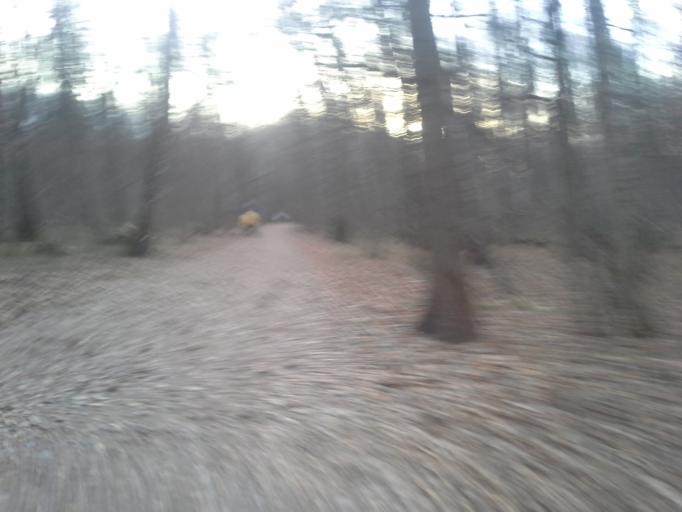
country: RU
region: Moscow
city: Chertanovo Yuzhnoye
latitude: 55.6189
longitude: 37.5746
